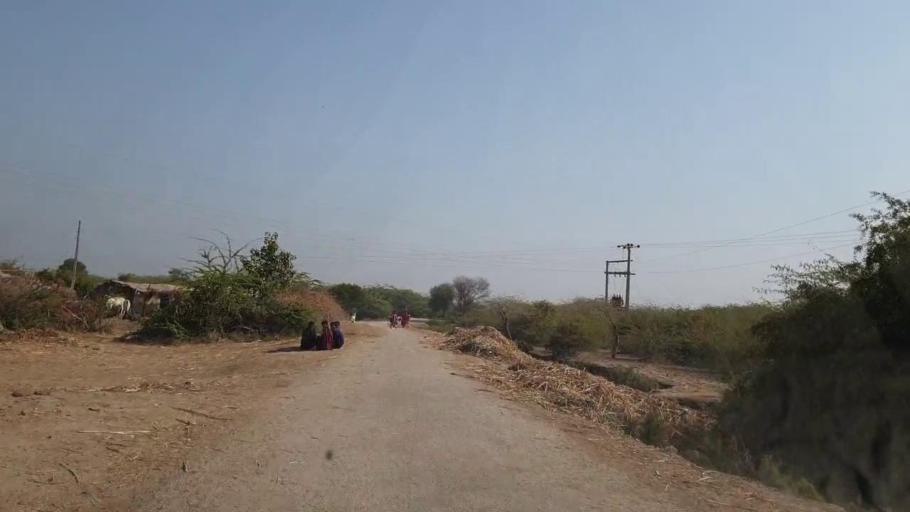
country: PK
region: Sindh
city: Mirpur Khas
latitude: 25.5929
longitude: 69.0031
